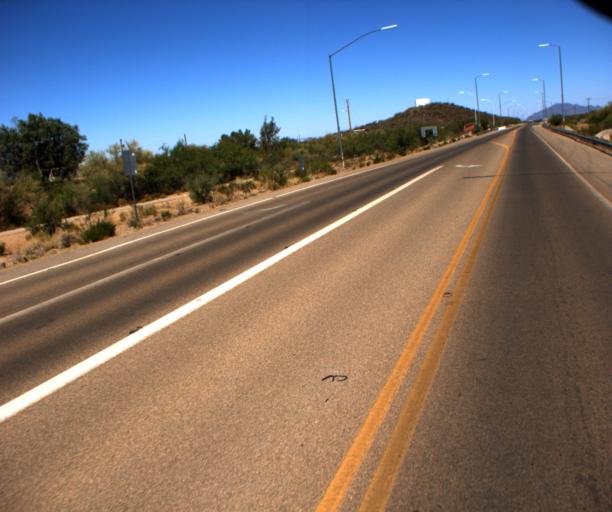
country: US
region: Arizona
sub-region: Pima County
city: Sells
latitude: 31.9187
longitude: -111.8804
